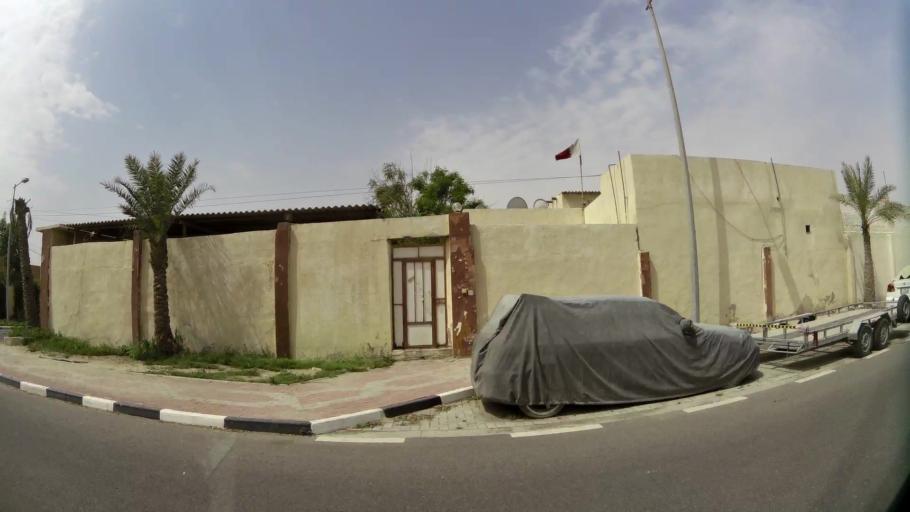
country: QA
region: Baladiyat ad Dawhah
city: Doha
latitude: 25.3136
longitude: 51.4837
